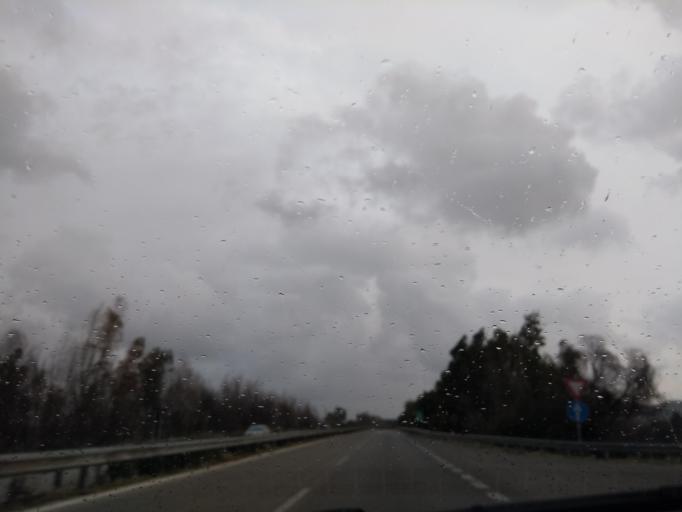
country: IT
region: Sicily
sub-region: Trapani
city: Erice
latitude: 38.0040
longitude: 12.5864
